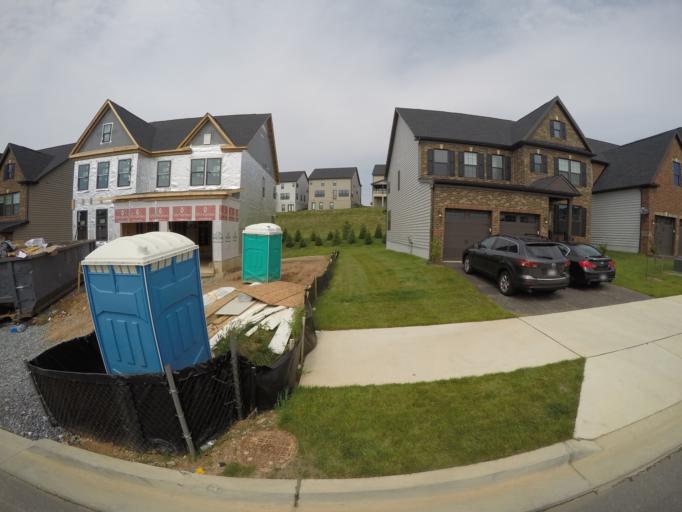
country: US
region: Maryland
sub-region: Montgomery County
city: Clarksburg
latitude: 39.2174
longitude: -77.2883
